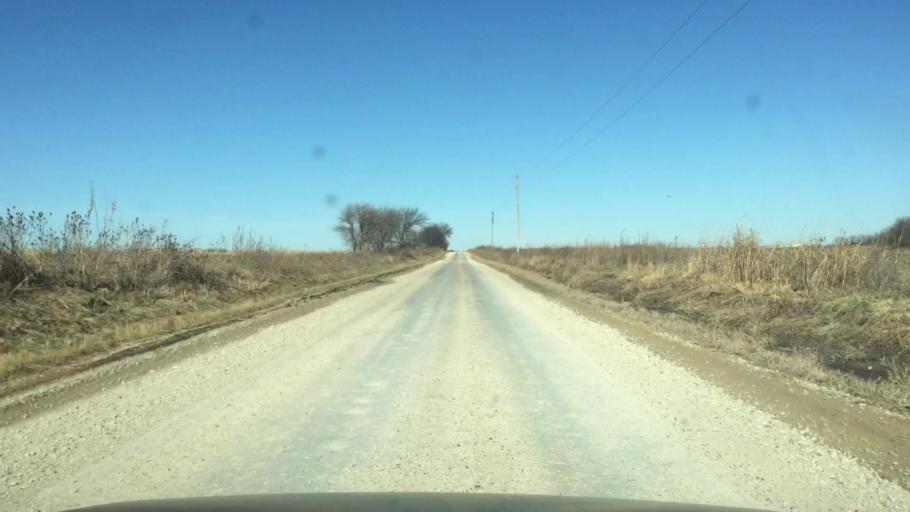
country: US
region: Kansas
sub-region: Allen County
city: Humboldt
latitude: 37.8535
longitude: -95.3910
